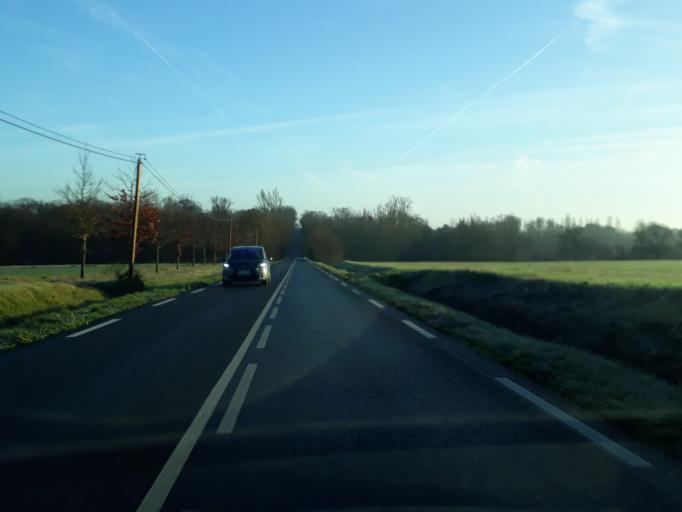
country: FR
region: Midi-Pyrenees
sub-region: Departement de la Haute-Garonne
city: Rieumes
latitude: 43.4168
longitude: 1.1325
